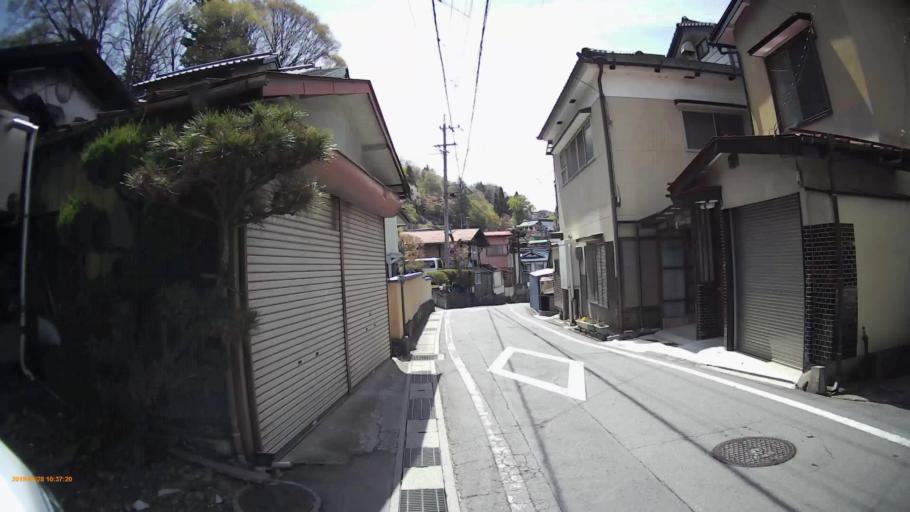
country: JP
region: Nagano
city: Suwa
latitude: 36.0533
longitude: 138.1184
